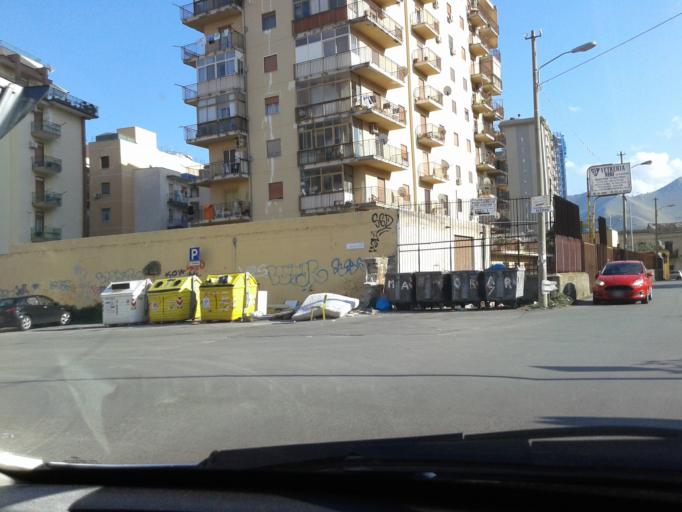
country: IT
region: Sicily
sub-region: Palermo
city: Monreale
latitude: 38.0991
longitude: 13.3178
